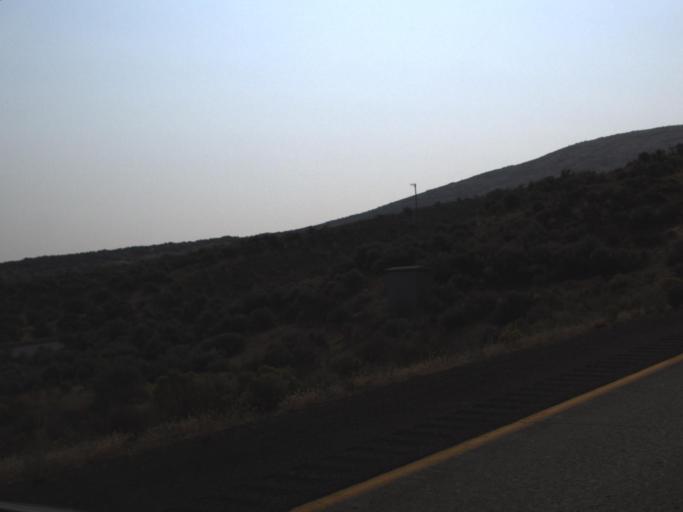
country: US
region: Washington
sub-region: Kittitas County
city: Kittitas
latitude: 46.8863
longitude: -120.4282
